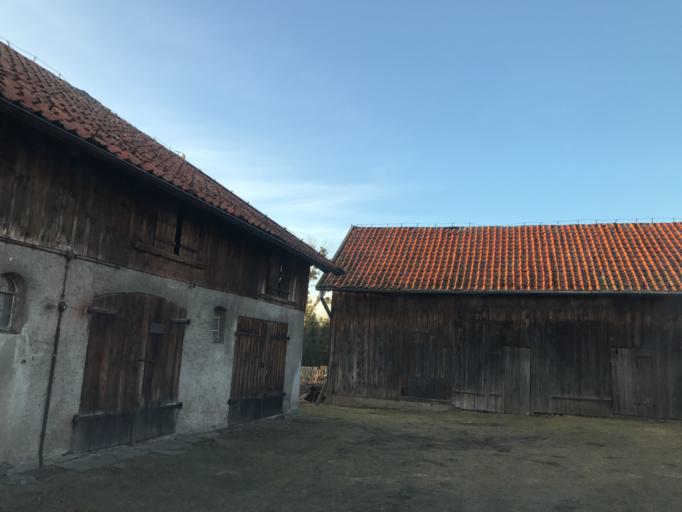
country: PL
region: Warmian-Masurian Voivodeship
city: Dobre Miasto
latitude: 54.0269
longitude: 20.4096
